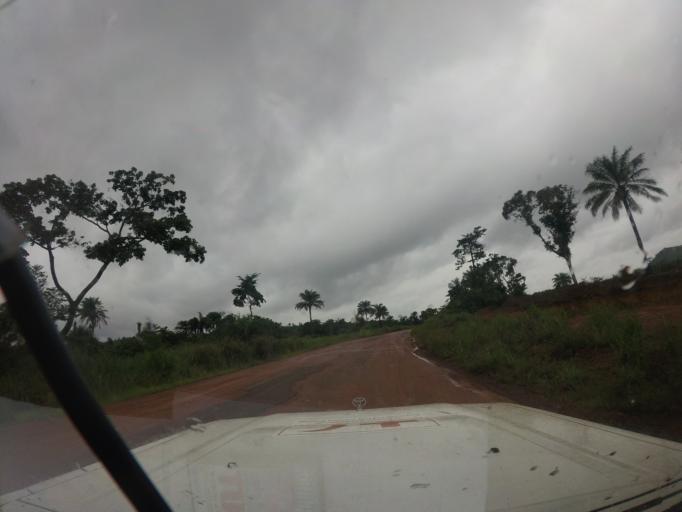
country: SL
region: Eastern Province
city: Tefeya
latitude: 8.5667
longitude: -11.2817
